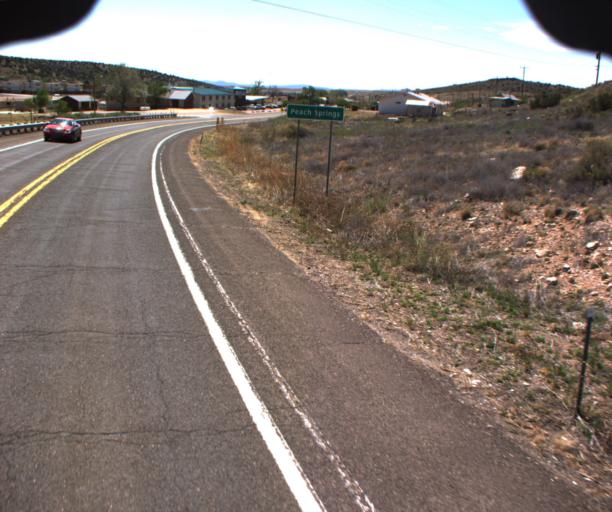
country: US
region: Arizona
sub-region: Mohave County
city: Peach Springs
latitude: 35.5301
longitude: -113.4219
